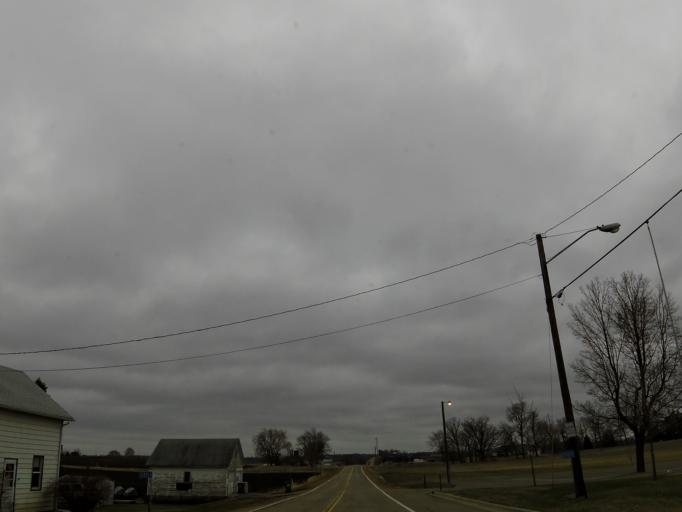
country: US
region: Minnesota
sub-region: Scott County
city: Shakopee
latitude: 44.7201
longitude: -93.5414
